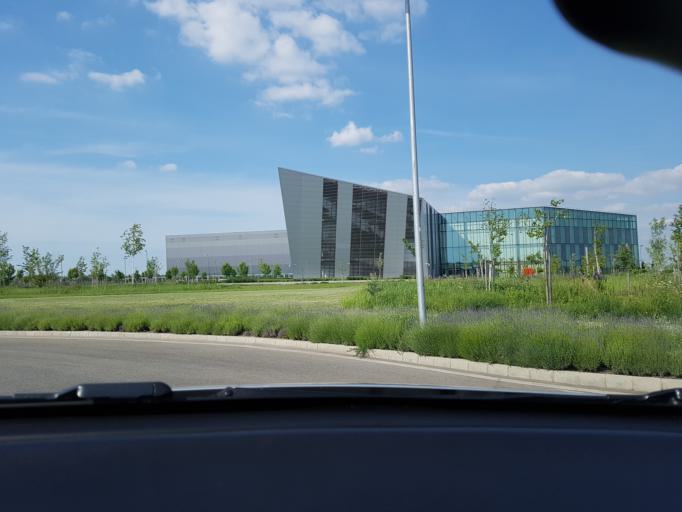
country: HU
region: Csongrad
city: Szeged
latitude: 46.2783
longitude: 20.1034
